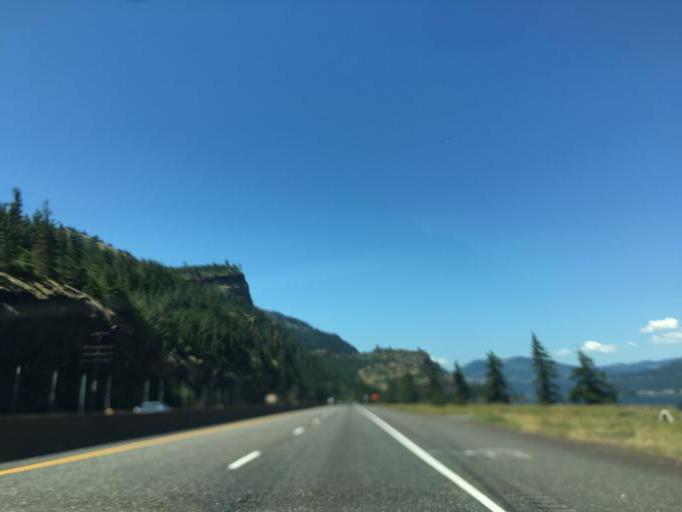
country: US
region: Washington
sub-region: Klickitat County
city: White Salmon
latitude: 45.6867
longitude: -121.4250
